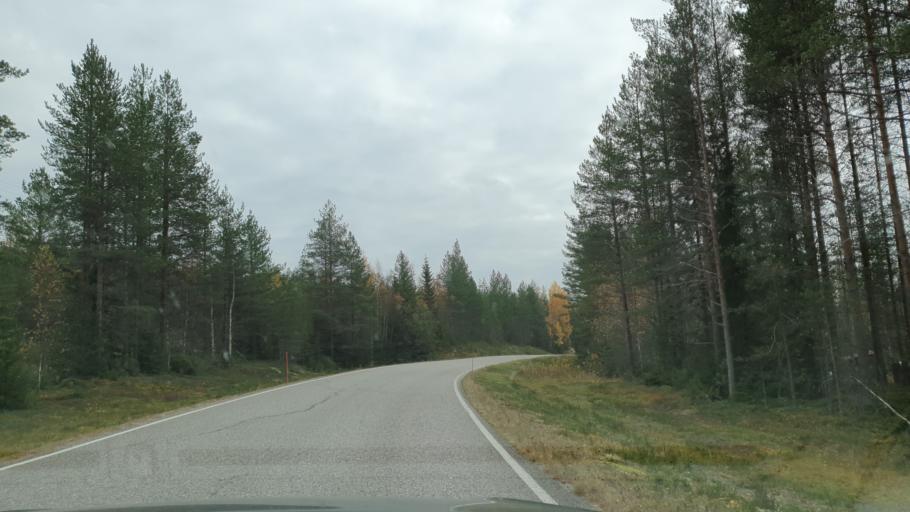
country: FI
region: Kainuu
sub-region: Kajaani
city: Ristijaervi
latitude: 64.6243
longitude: 27.9941
